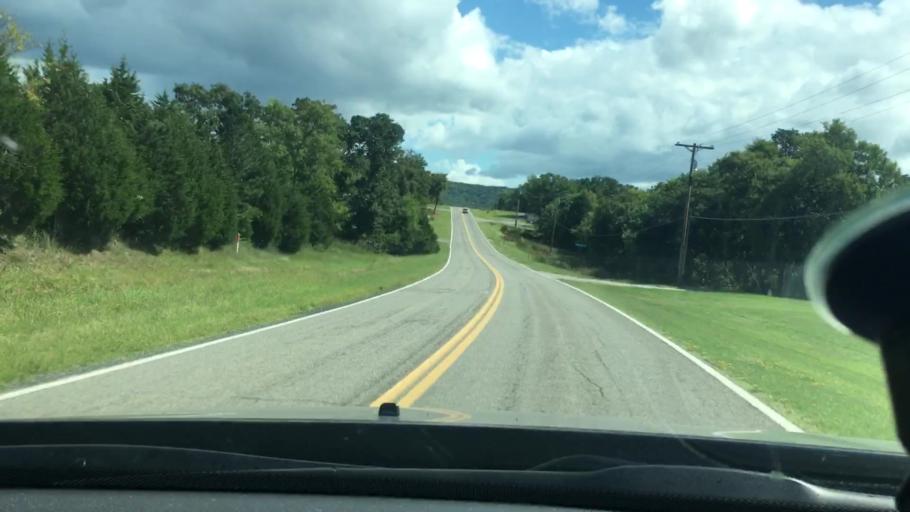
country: US
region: Oklahoma
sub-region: Cherokee County
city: Park Hill
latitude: 35.6940
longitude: -94.9141
